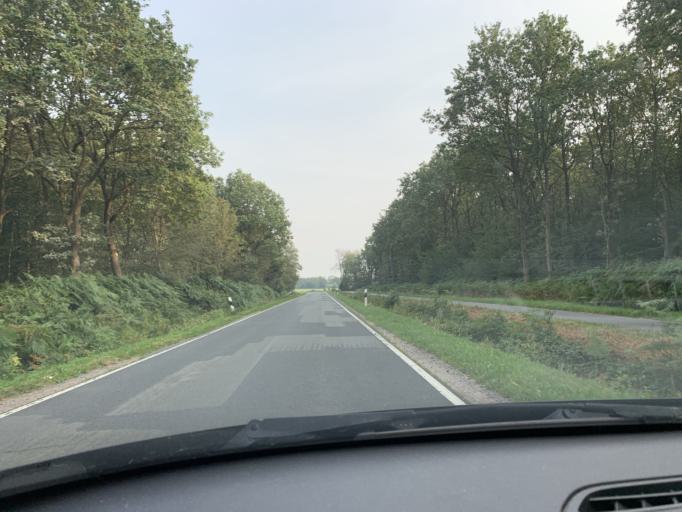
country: DE
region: Lower Saxony
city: Apen
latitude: 53.2559
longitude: 7.8471
